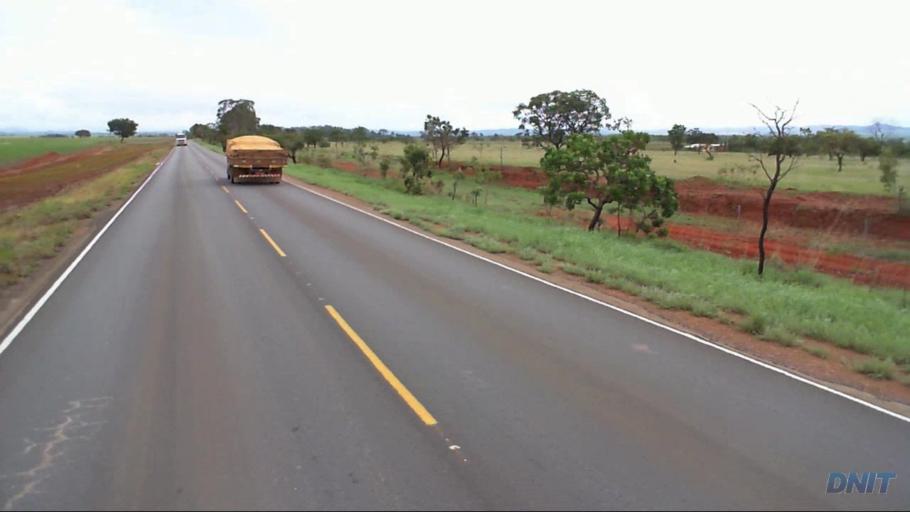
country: BR
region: Goias
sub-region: Padre Bernardo
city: Padre Bernardo
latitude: -15.3368
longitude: -48.2336
